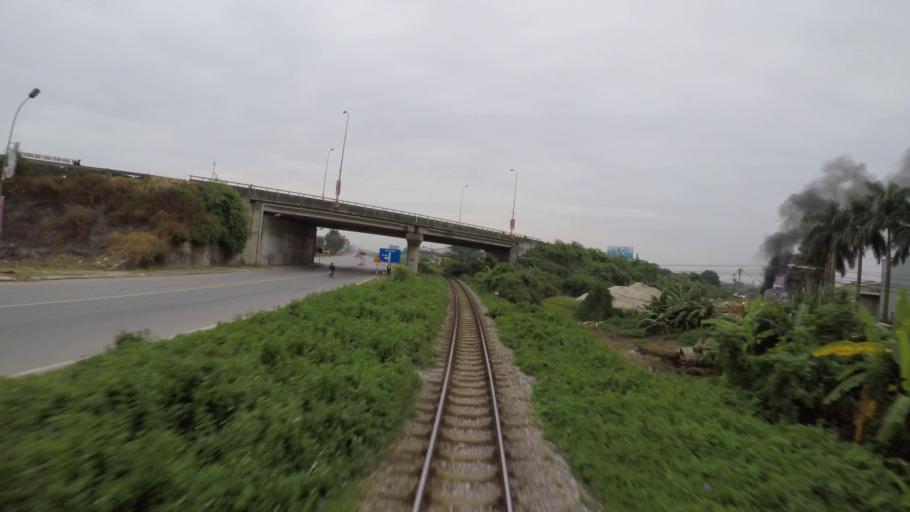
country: VN
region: Hung Yen
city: Nhu Quynh
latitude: 20.9797
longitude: 106.0189
